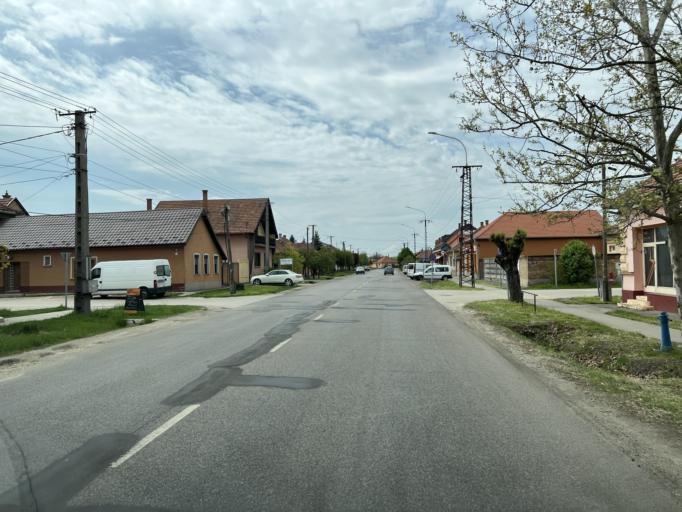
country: HU
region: Pest
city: Cegled
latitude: 47.1647
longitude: 19.8020
